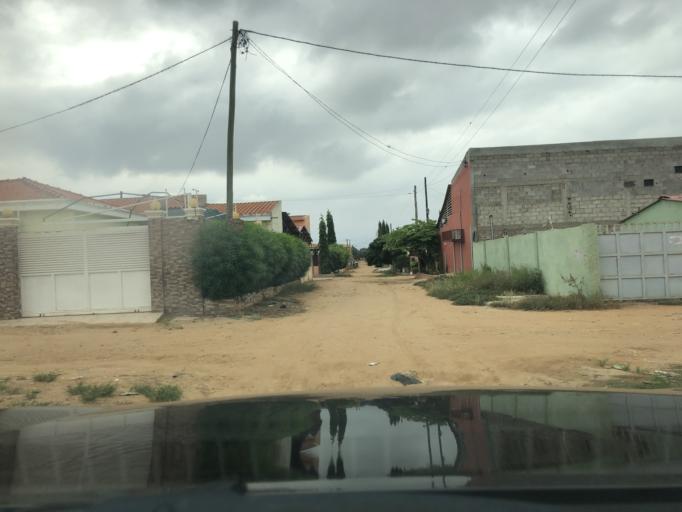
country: AO
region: Luanda
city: Luanda
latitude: -8.9369
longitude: 13.2533
